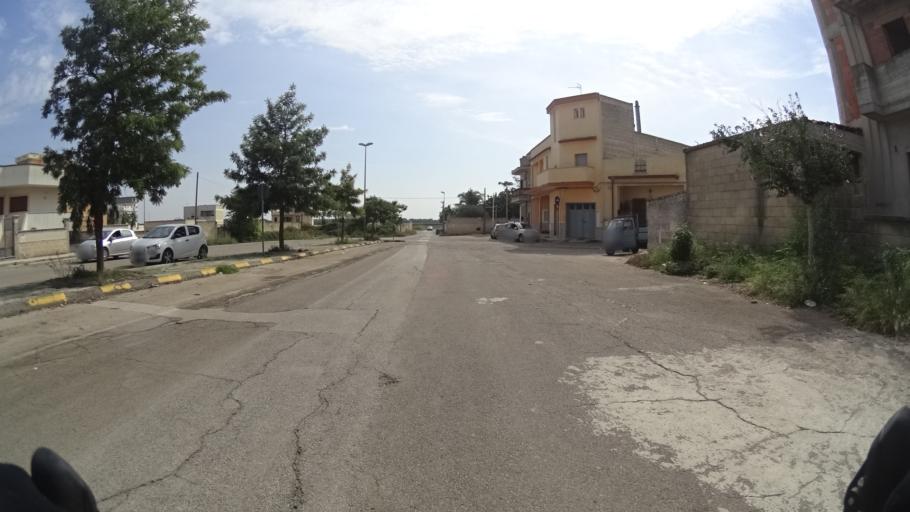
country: IT
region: Apulia
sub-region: Provincia di Taranto
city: San Marzano di San Giuseppe
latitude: 40.4499
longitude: 17.5104
